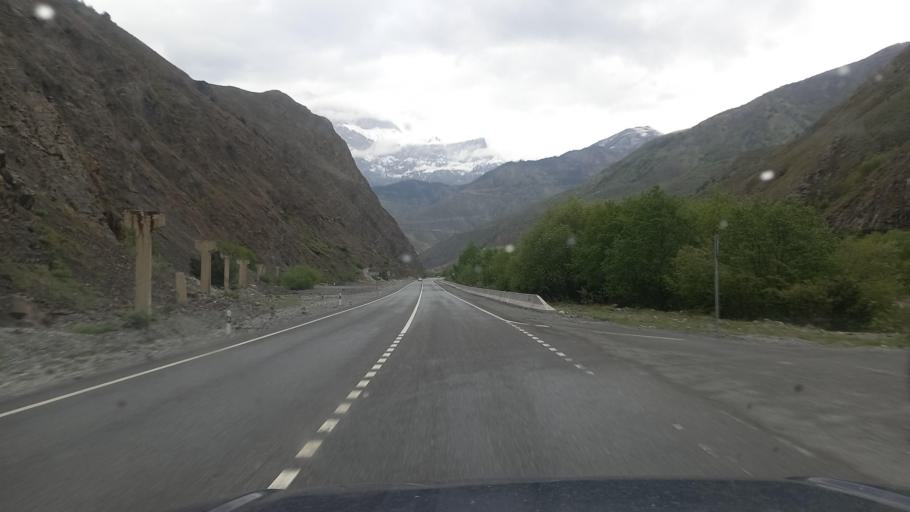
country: RU
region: North Ossetia
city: Mizur
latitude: 42.8573
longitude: 44.1115
